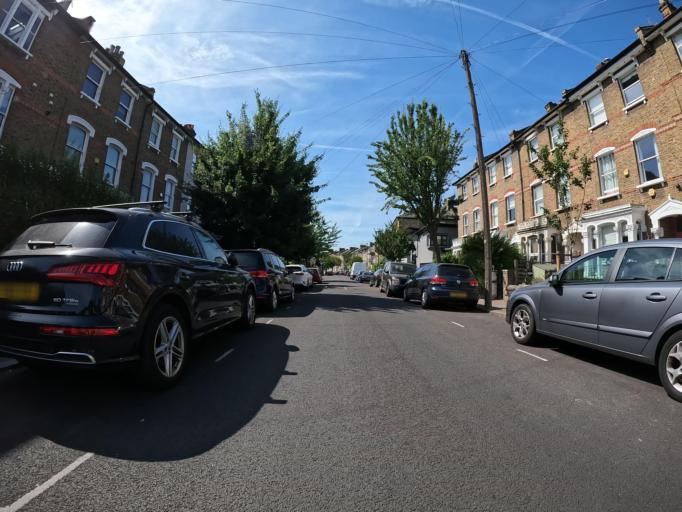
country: GB
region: England
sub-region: Greater London
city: Harringay
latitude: 51.5623
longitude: -0.1032
